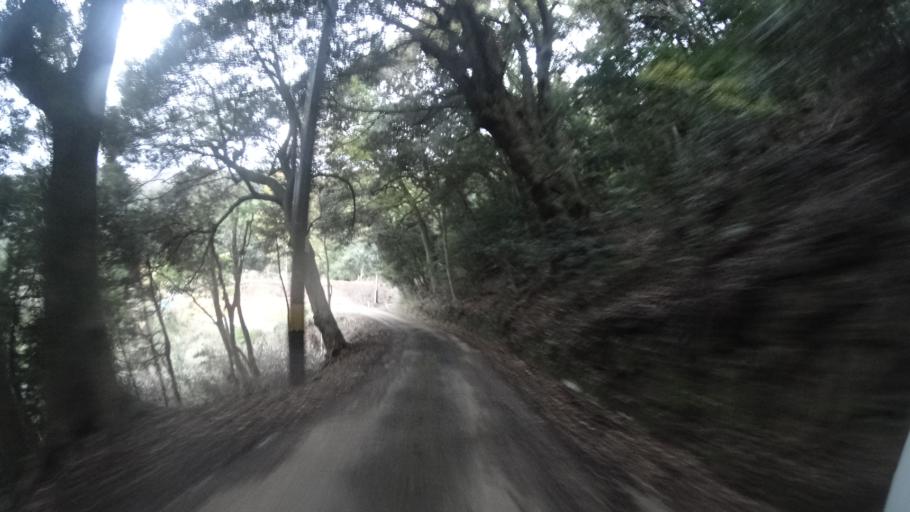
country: JP
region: Kyoto
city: Maizuru
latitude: 35.5633
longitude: 135.4630
